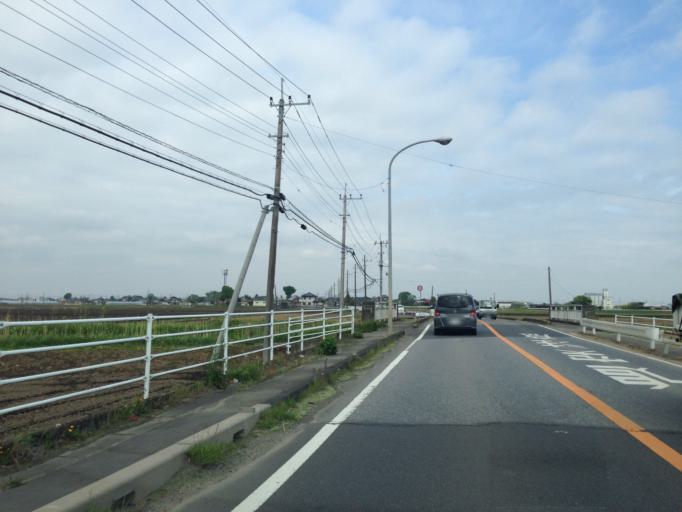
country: JP
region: Ibaraki
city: Ishige
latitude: 36.1512
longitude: 139.9910
